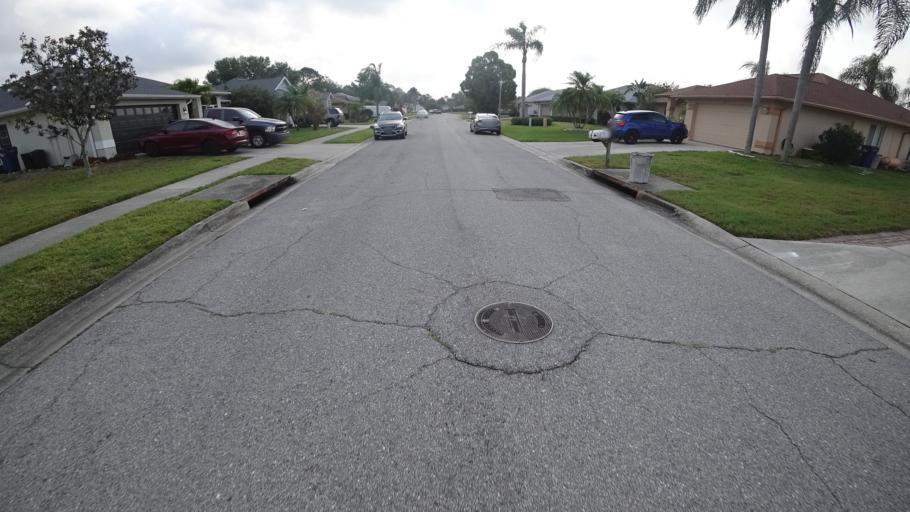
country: US
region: Florida
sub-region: Manatee County
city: Samoset
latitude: 27.4395
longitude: -82.5286
